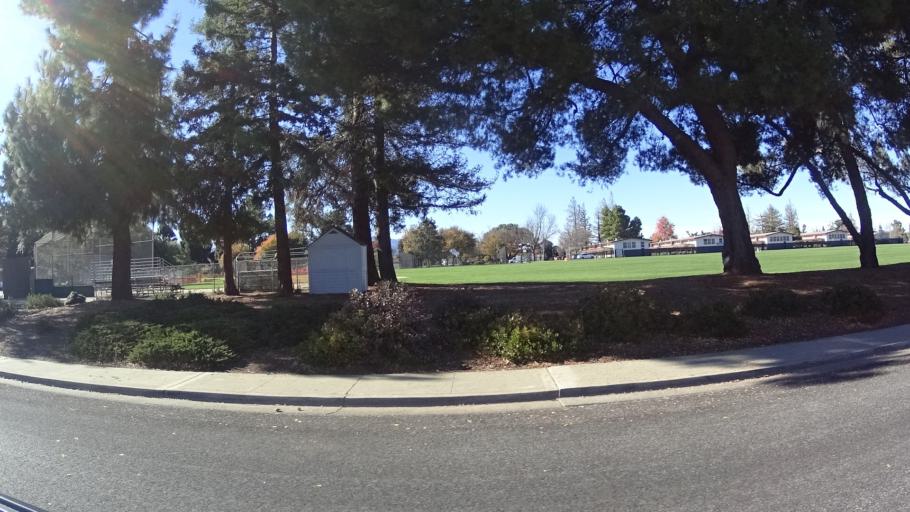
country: US
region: California
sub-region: Santa Clara County
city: Cupertino
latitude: 37.3439
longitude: -122.0054
